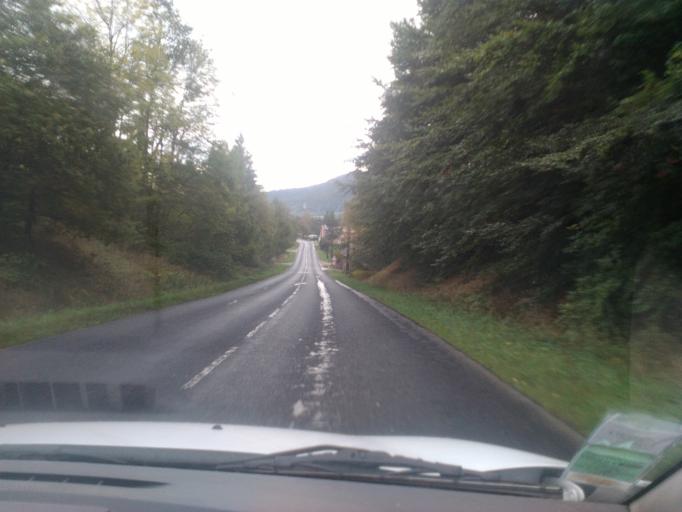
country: FR
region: Lorraine
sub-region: Departement des Vosges
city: Granges-sur-Vologne
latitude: 48.1894
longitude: 6.7709
